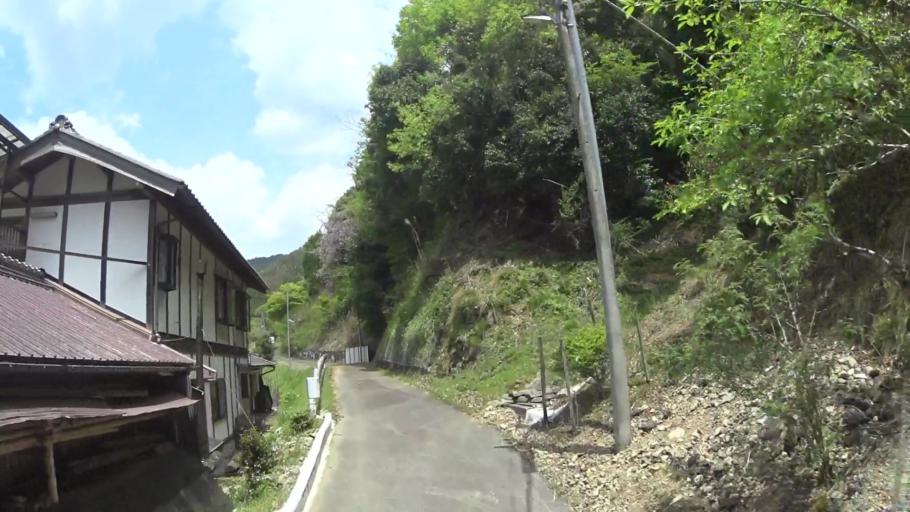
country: JP
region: Kyoto
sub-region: Kyoto-shi
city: Kamigyo-ku
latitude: 35.1235
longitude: 135.7011
